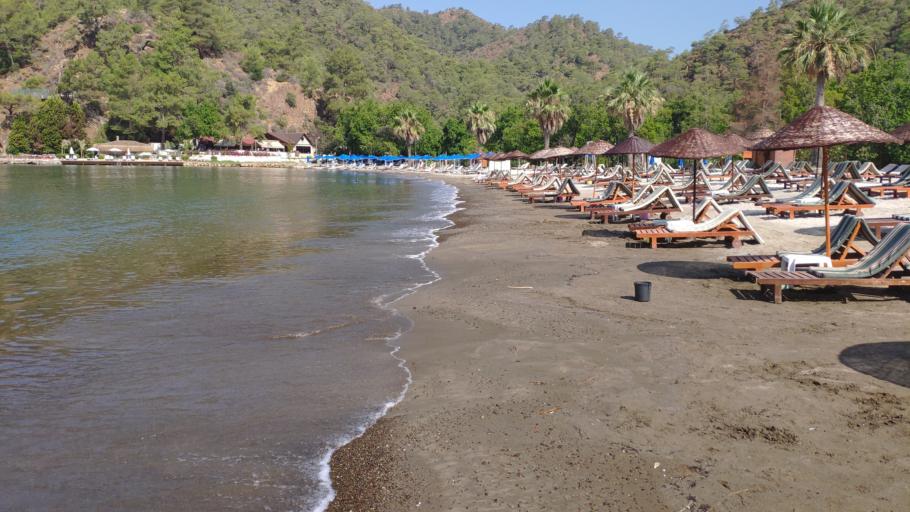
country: TR
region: Mugla
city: Yaniklar
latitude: 36.7155
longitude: 29.0205
